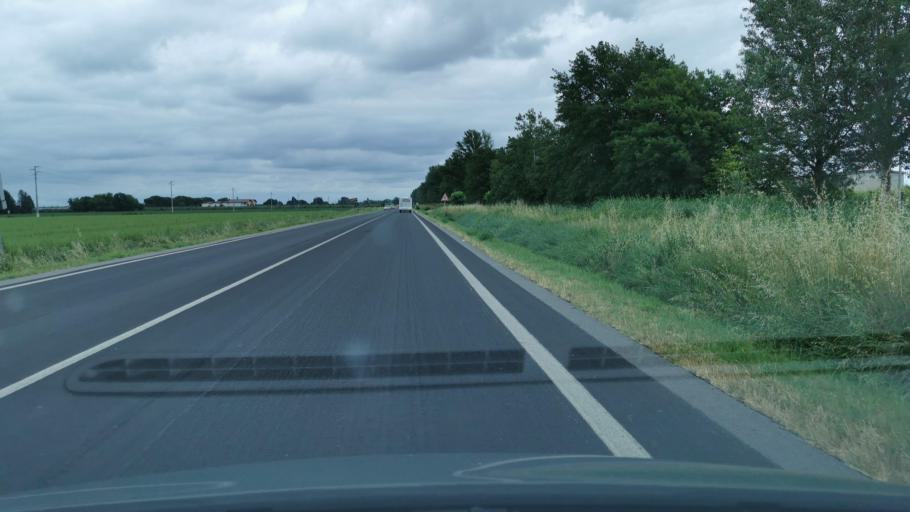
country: IT
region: Emilia-Romagna
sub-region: Provincia di Ravenna
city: Granarolo
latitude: 44.3367
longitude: 11.9167
